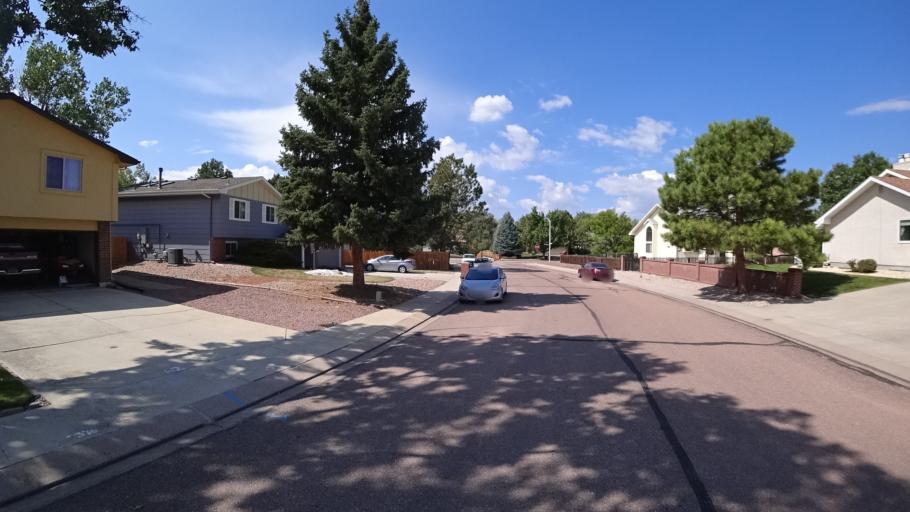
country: US
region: Colorado
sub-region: El Paso County
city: Cimarron Hills
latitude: 38.8611
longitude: -104.7282
